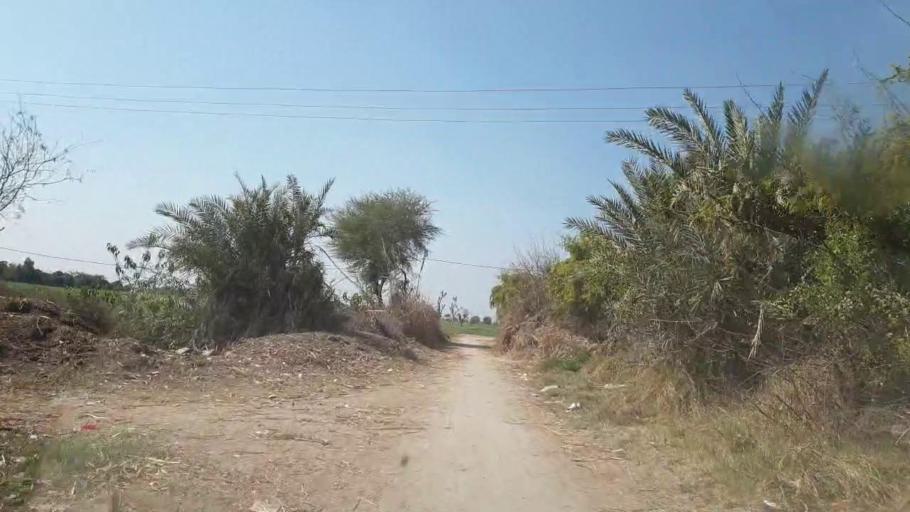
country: PK
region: Sindh
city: Mirpur Khas
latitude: 25.7355
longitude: 69.0979
